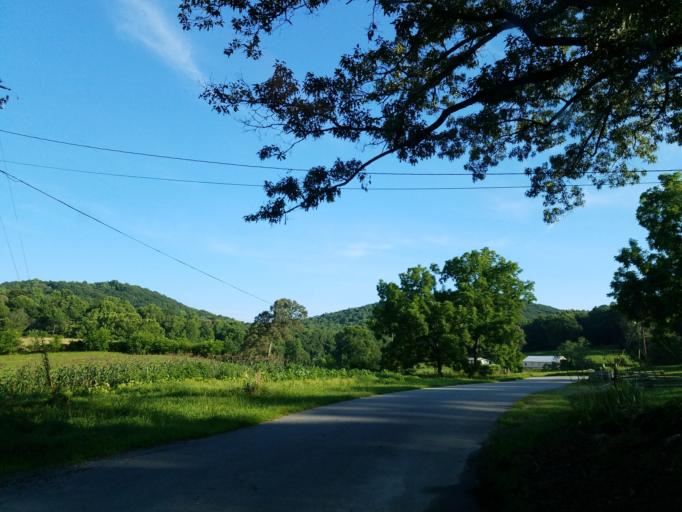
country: US
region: Georgia
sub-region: Gilmer County
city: Ellijay
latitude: 34.6321
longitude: -84.3315
